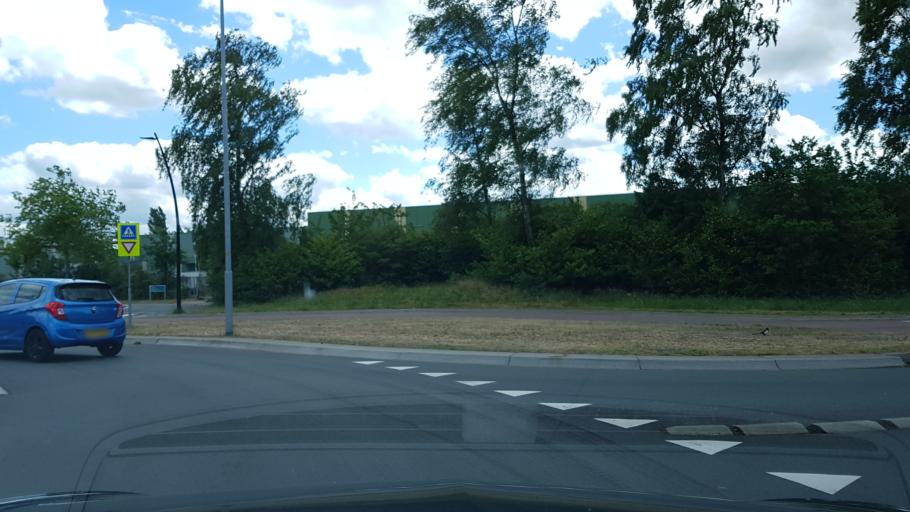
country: NL
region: Gelderland
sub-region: Gemeente Harderwijk
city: Harderwijk
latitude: 52.3407
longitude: 5.6151
